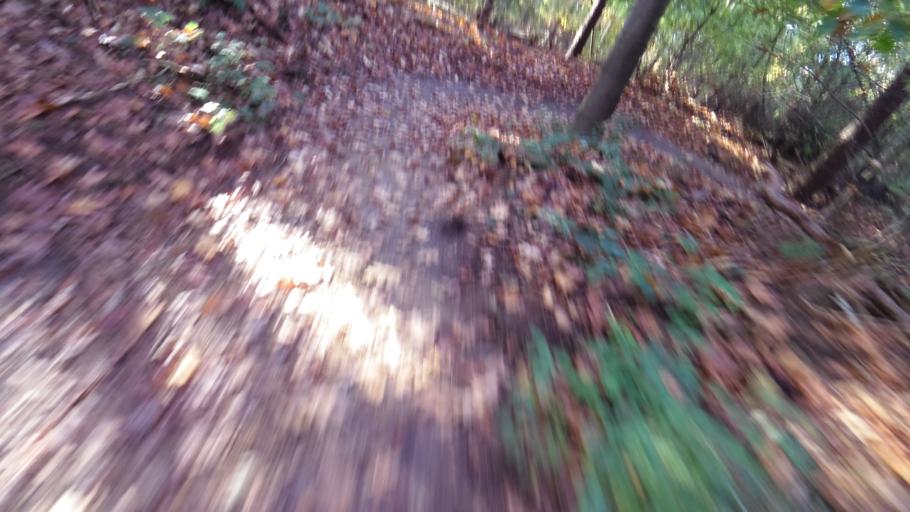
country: NL
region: Gelderland
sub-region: Gemeente Ede
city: Ede
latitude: 52.0678
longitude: 5.6623
